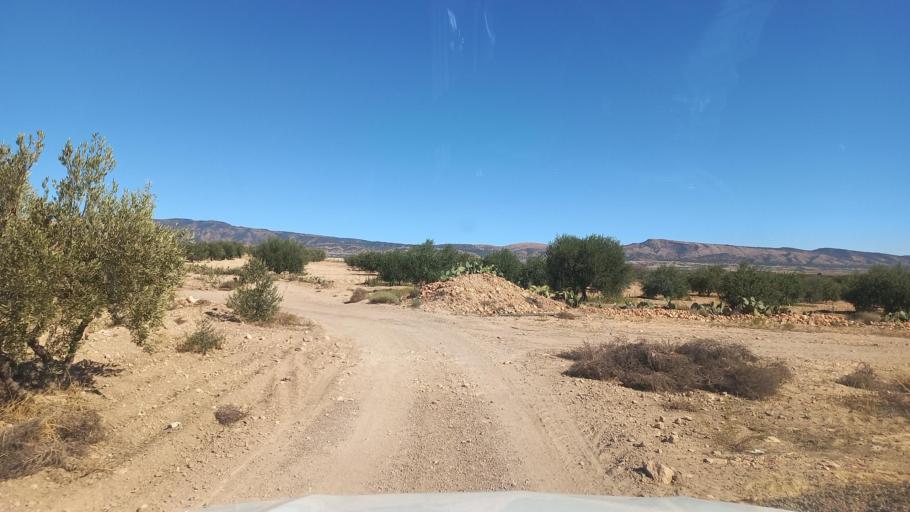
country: TN
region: Al Qasrayn
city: Sbiba
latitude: 35.3987
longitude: 9.0851
